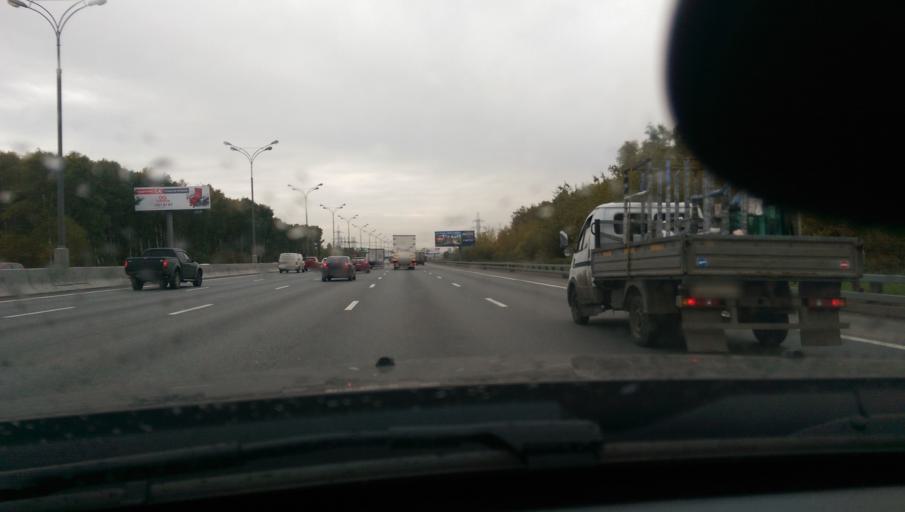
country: RU
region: Moscow
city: Vatutino
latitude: 55.8964
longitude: 37.6540
